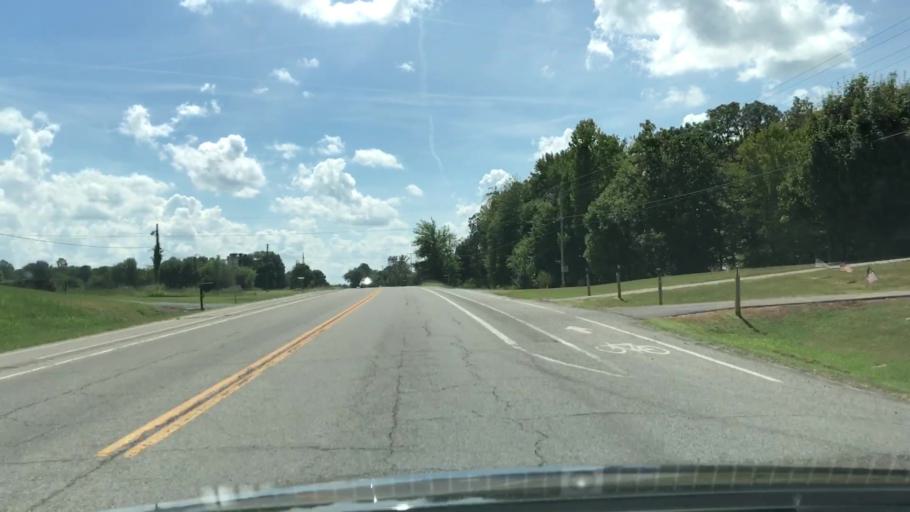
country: US
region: Tennessee
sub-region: Sumner County
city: White House
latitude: 36.5072
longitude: -86.6422
